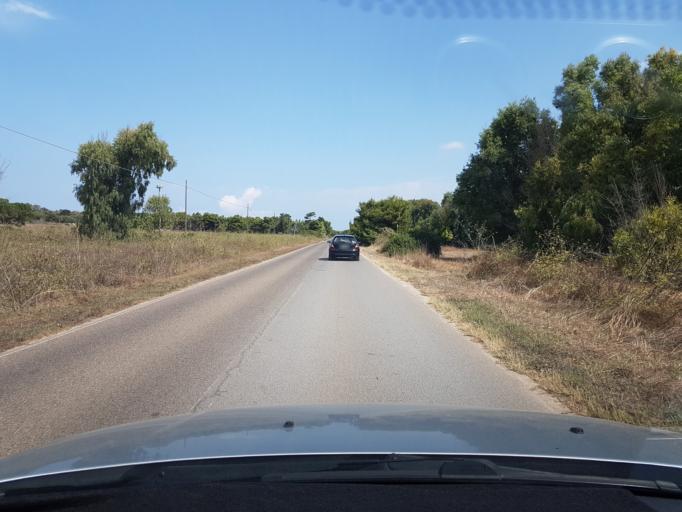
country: IT
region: Sardinia
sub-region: Provincia di Oristano
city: Cabras
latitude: 39.8907
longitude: 8.4350
